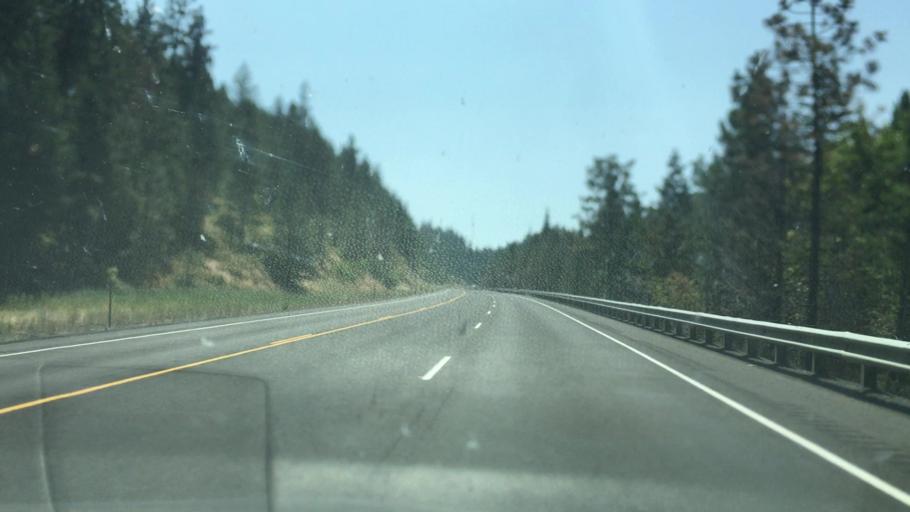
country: US
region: Idaho
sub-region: Idaho County
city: Grangeville
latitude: 45.8628
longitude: -116.2370
